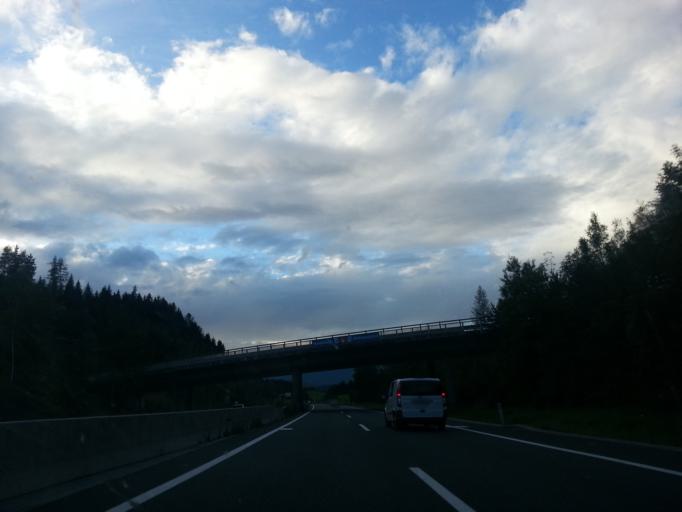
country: AT
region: Upper Austria
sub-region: Politischer Bezirk Kirchdorf an der Krems
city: Rossleithen
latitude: 47.6841
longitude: 14.3235
